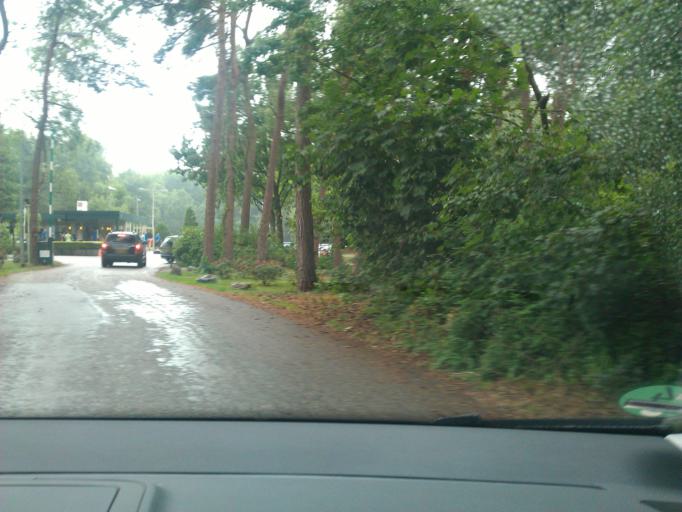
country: NL
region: North Brabant
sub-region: Gemeente Bladel en Netersel
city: Bladel
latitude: 51.3439
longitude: 5.2507
